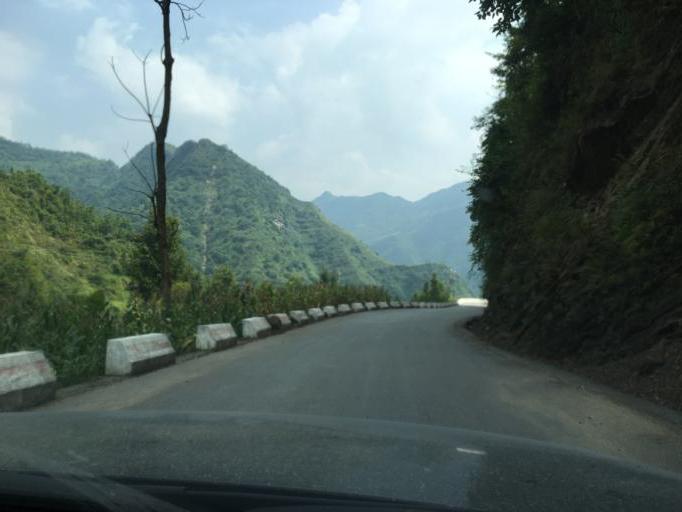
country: CN
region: Guangxi Zhuangzu Zizhiqu
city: Tongle
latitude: 25.2942
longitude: 106.2633
